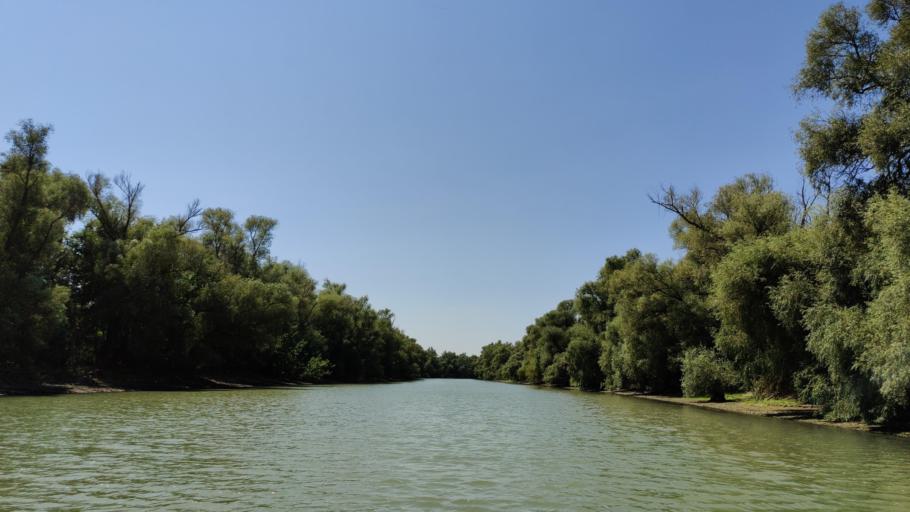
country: RO
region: Tulcea
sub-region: Comuna Pardina
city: Pardina
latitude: 45.2356
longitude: 28.9155
